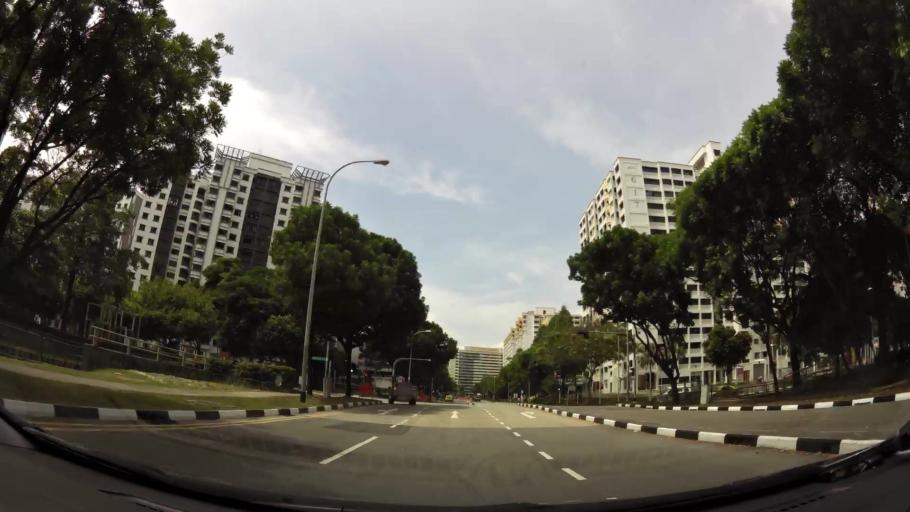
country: MY
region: Johor
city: Johor Bahru
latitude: 1.3406
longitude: 103.7013
